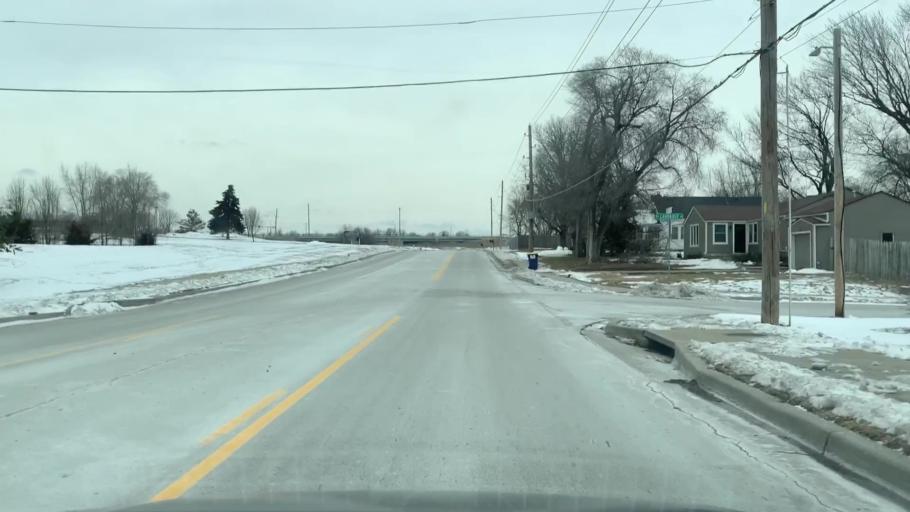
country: US
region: Missouri
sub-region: Jackson County
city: Lees Summit
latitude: 38.9425
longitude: -94.3643
